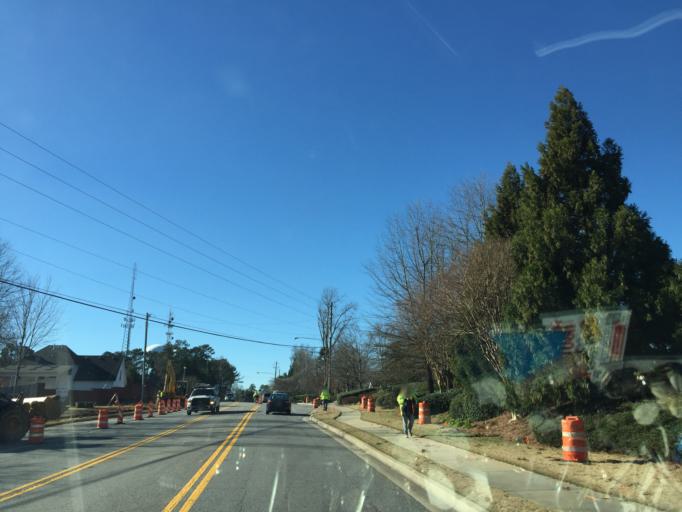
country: US
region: Georgia
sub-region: Fulton County
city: Johns Creek
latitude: 34.0447
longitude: -84.2250
